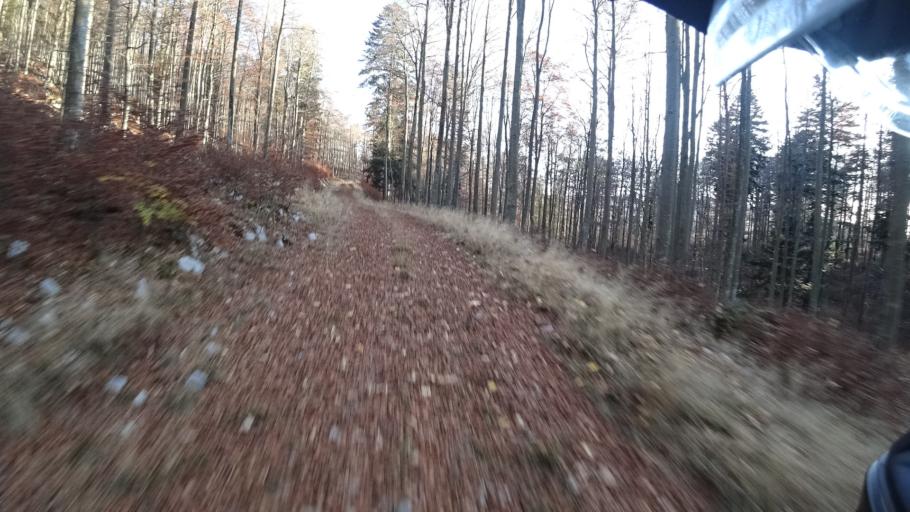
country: HR
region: Primorsko-Goranska
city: Drazice
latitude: 45.4855
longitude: 14.4840
